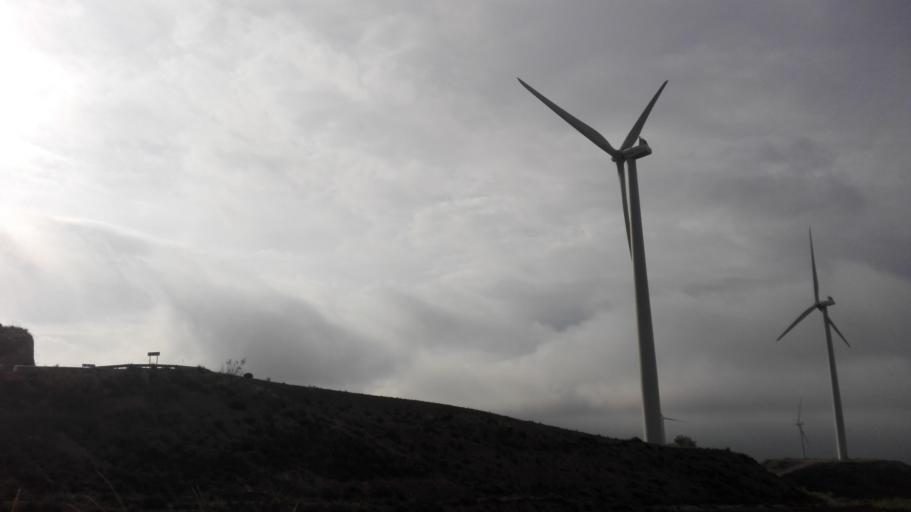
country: ES
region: Andalusia
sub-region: Provincia de Granada
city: Lanjaron
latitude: 36.9139
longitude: -3.5133
